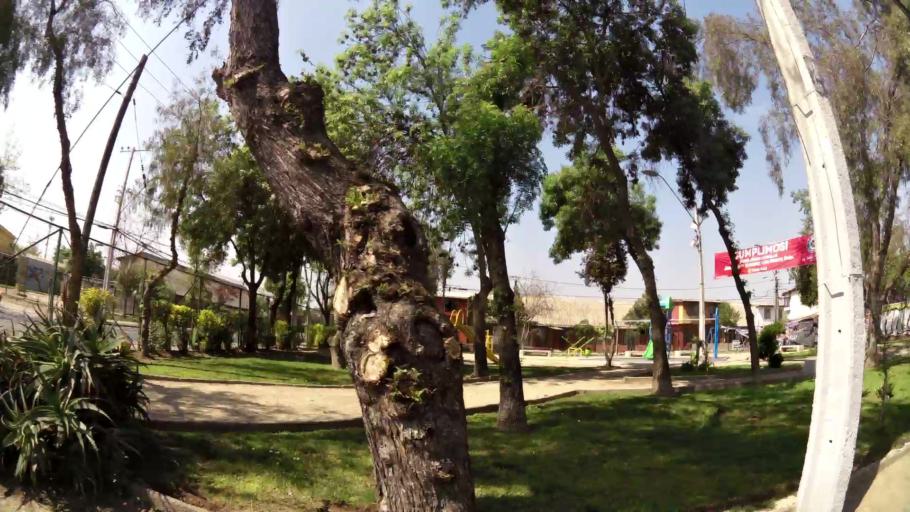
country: CL
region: Santiago Metropolitan
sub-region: Provincia de Santiago
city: La Pintana
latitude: -33.5506
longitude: -70.6120
